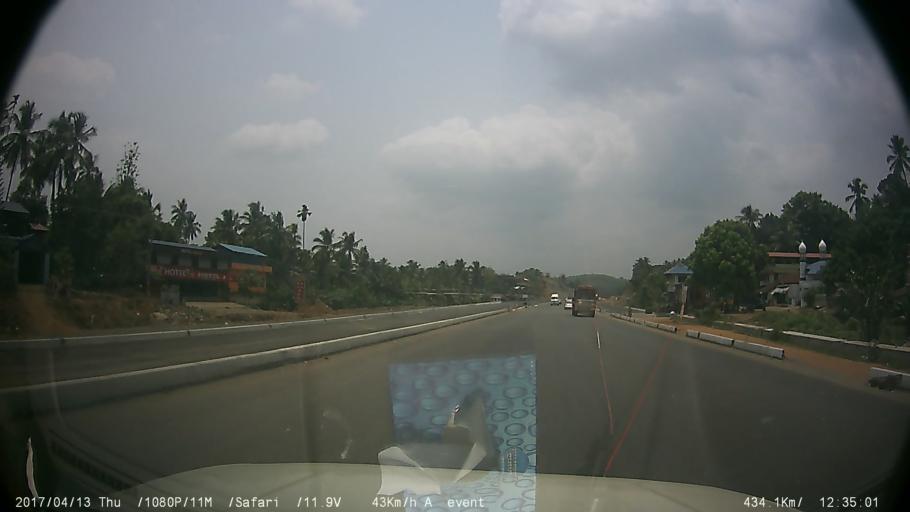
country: IN
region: Kerala
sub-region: Thrissur District
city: Chelakara
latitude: 10.5606
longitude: 76.3457
